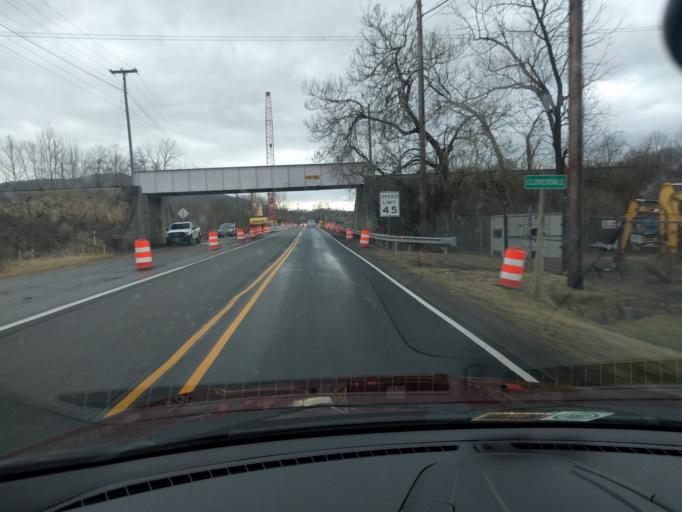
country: US
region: Virginia
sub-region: Botetourt County
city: Cloverdale
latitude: 37.3747
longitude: -79.9049
